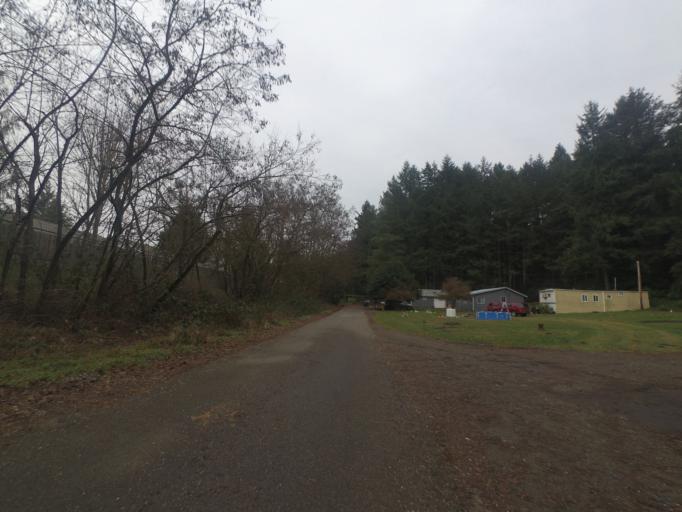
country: US
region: Washington
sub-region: Pierce County
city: McChord Air Force Base
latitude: 47.1249
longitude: -122.5239
